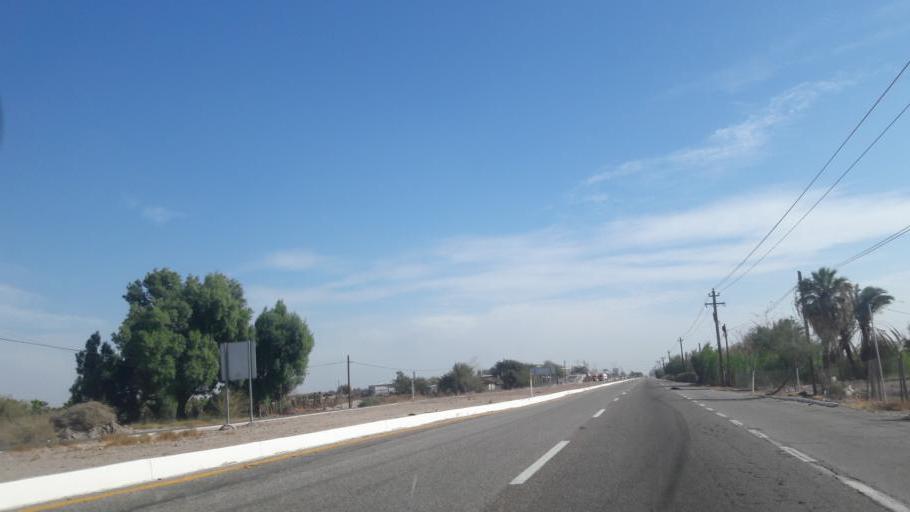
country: MX
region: Baja California
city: Progreso
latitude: 32.6015
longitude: -115.6550
